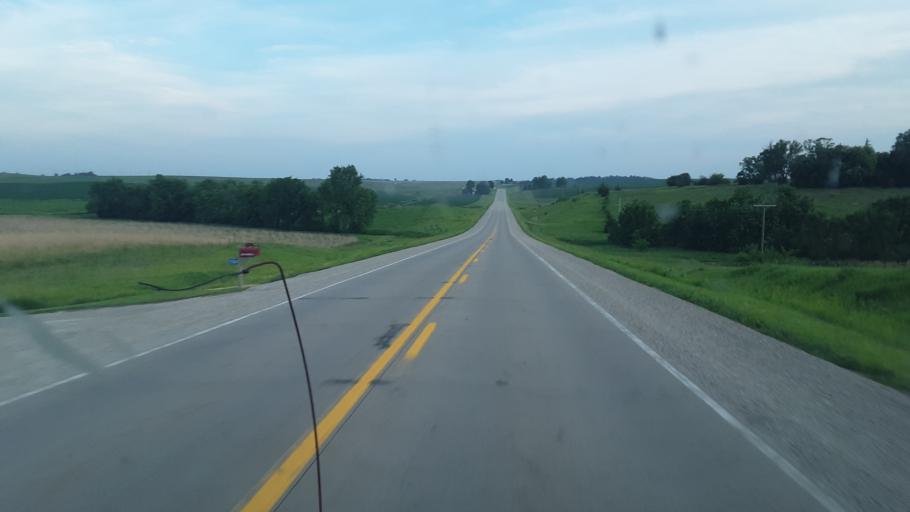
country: US
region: Iowa
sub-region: Benton County
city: Belle Plaine
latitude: 41.7880
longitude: -92.2792
